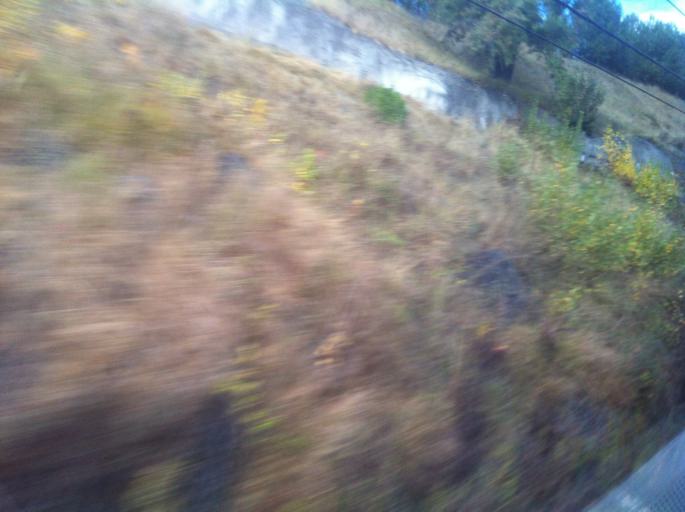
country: ES
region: Basque Country
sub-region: Provincia de Alava
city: Arminon
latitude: 42.7172
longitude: -2.8763
